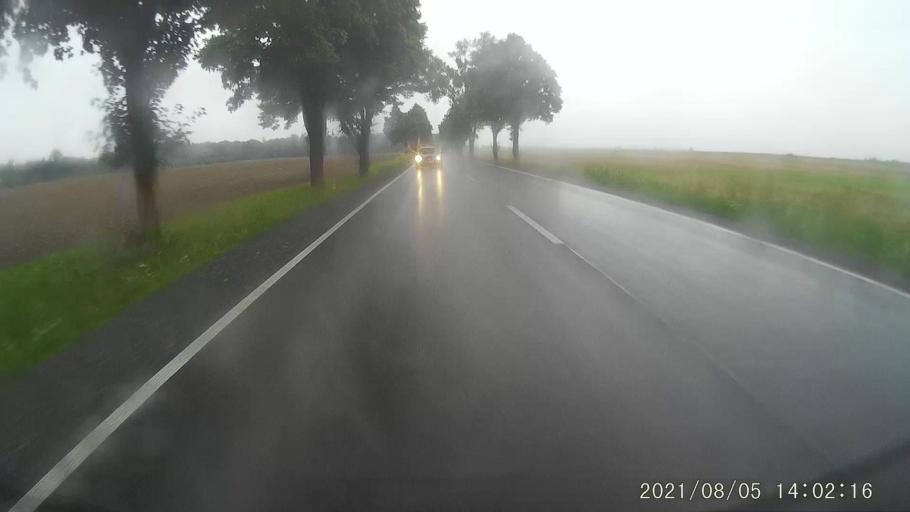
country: PL
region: Opole Voivodeship
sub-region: Powiat krapkowicki
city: Strzeleczki
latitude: 50.4543
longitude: 17.8781
